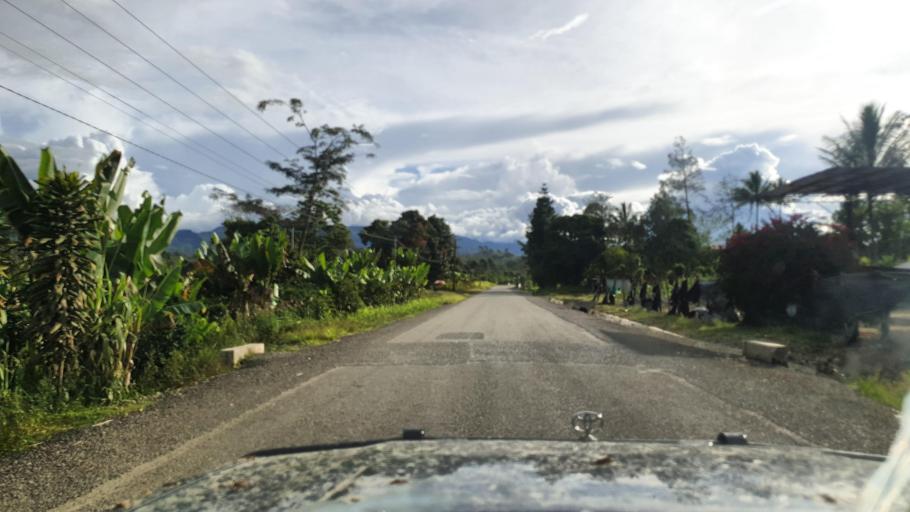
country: PG
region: Jiwaka
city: Minj
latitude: -5.8769
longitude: 144.7071
